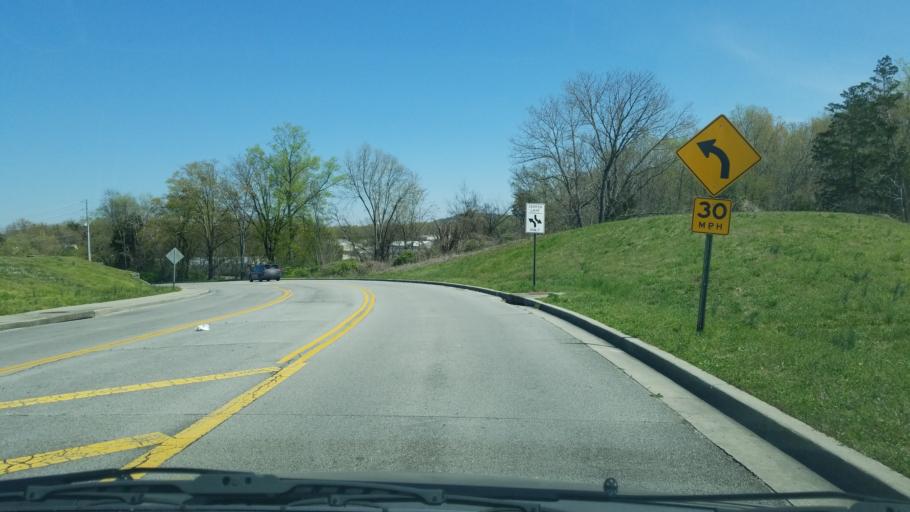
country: US
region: Tennessee
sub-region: Hamilton County
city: Red Bank
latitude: 35.1290
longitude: -85.2347
